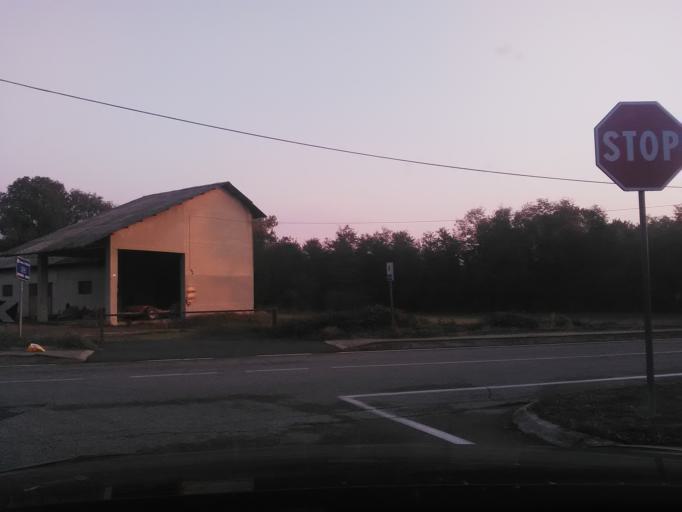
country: IT
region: Piedmont
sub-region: Provincia di Vercelli
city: Rovasenda
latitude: 45.5366
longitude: 8.3082
